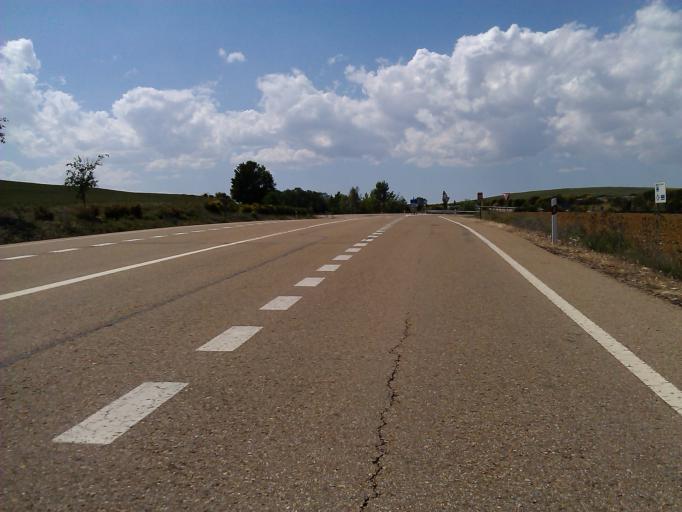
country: ES
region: Castille and Leon
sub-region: Provincia de Palencia
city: Ledigos
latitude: 42.3656
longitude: -4.8731
